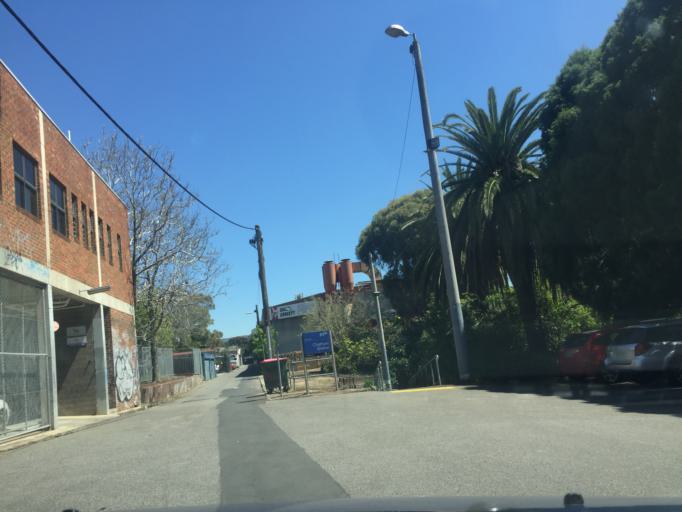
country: AU
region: Victoria
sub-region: Boroondara
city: Canterbury
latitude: -37.8245
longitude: 145.0891
